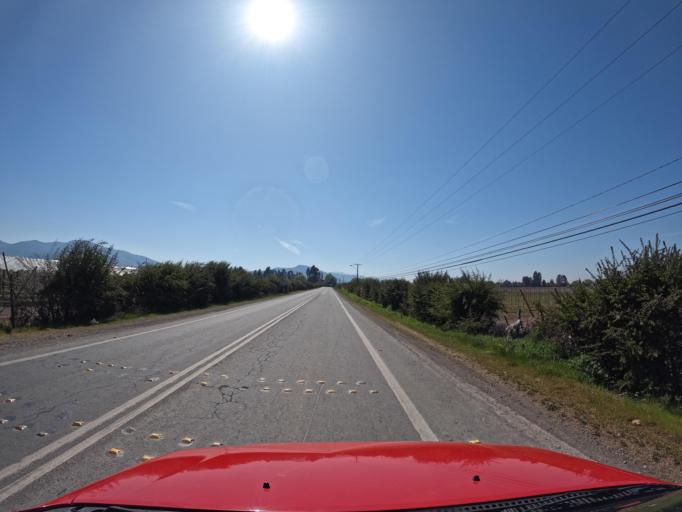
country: CL
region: Maule
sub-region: Provincia de Curico
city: Rauco
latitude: -35.0068
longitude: -71.4021
